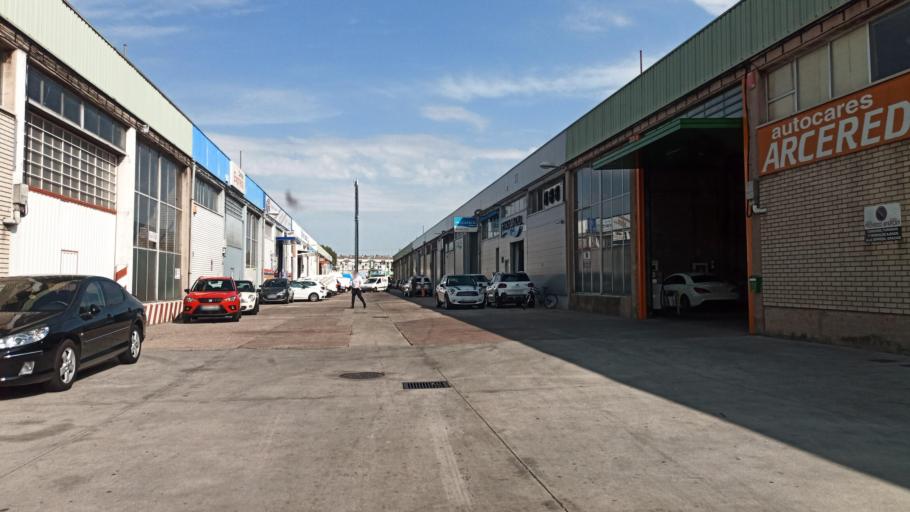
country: ES
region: Castille and Leon
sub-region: Provincia de Burgos
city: Burgos
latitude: 42.3579
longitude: -3.6555
